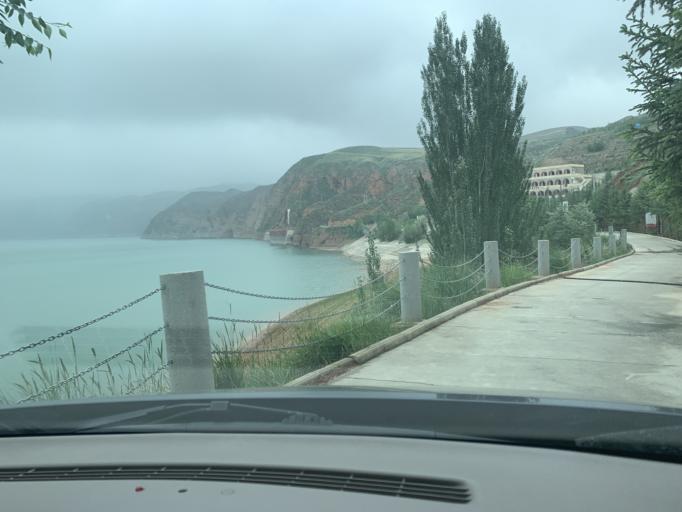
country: CN
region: Gansu Sheng
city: Gulang
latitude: 37.5614
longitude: 102.7424
